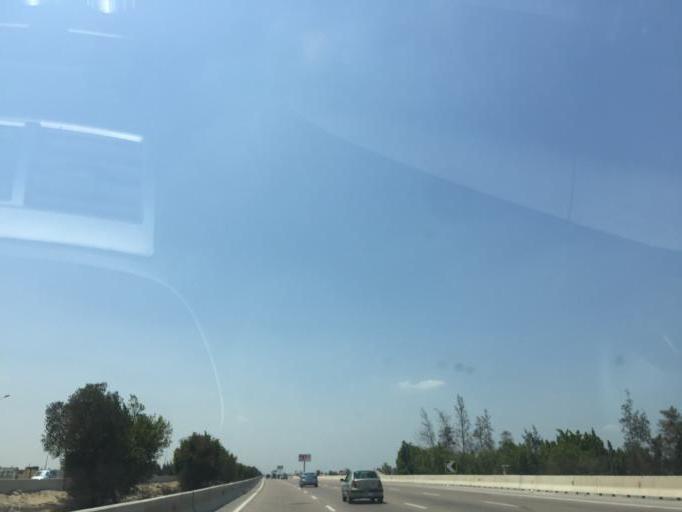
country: EG
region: Al Buhayrah
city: Beheira
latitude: 30.4432
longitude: 30.3261
